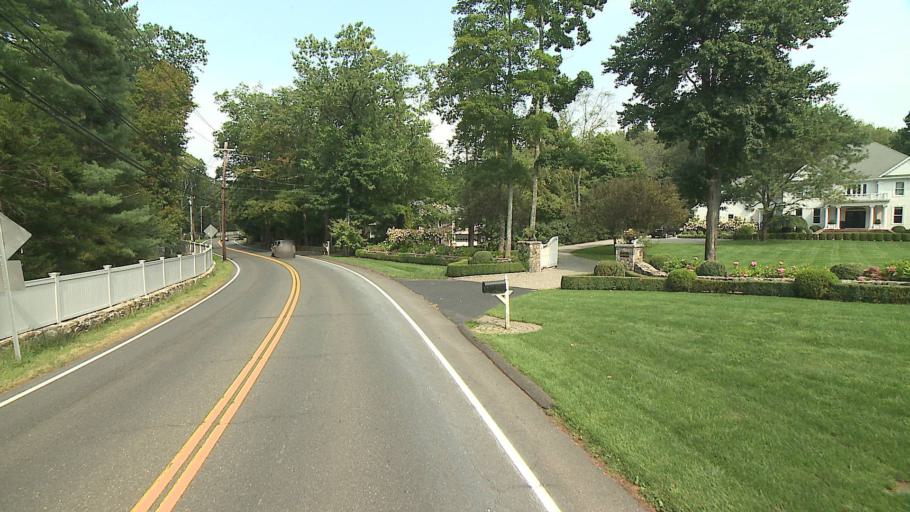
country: US
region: Connecticut
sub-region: Fairfield County
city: Ridgefield
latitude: 41.2699
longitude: -73.4800
